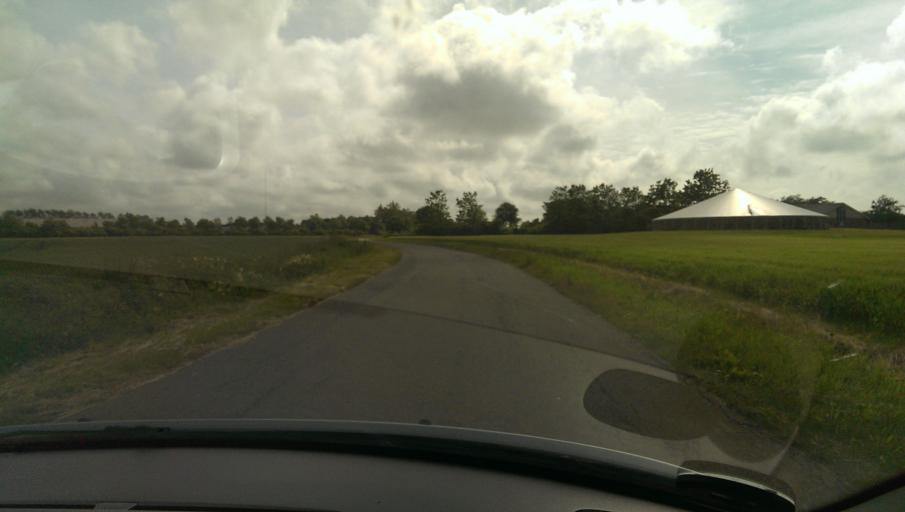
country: DK
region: Central Jutland
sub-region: Holstebro Kommune
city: Ulfborg
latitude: 56.2785
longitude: 8.2723
